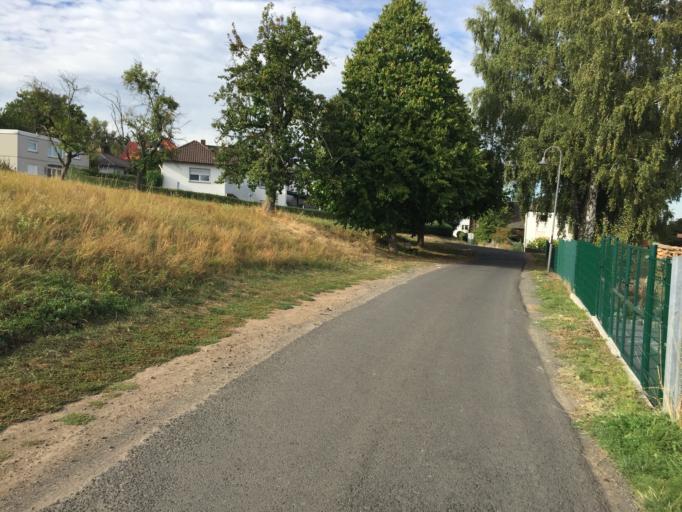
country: DE
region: Hesse
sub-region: Regierungsbezirk Giessen
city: Langgons
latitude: 50.5107
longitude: 8.7271
